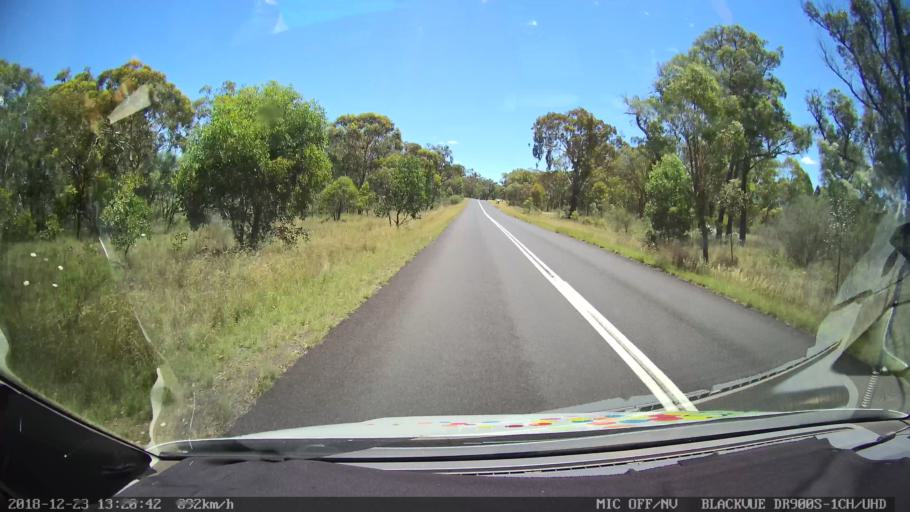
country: AU
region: New South Wales
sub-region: Armidale Dumaresq
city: Armidale
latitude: -30.4838
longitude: 151.4459
